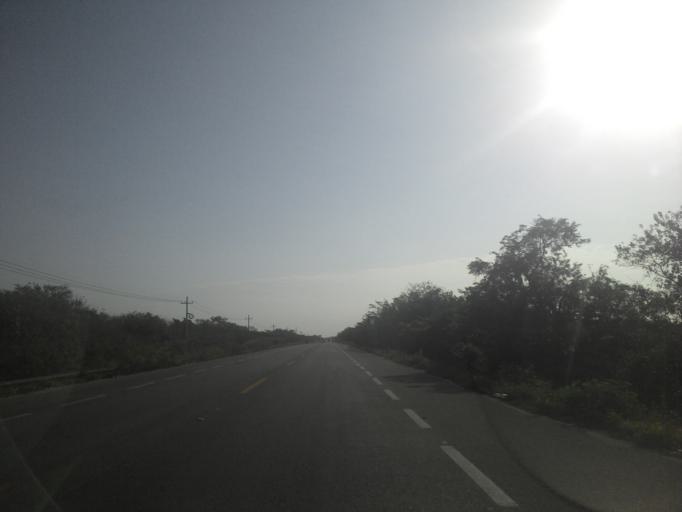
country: MX
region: Yucatan
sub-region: Valladolid
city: Tesoco
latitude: 20.6982
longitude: -88.1420
